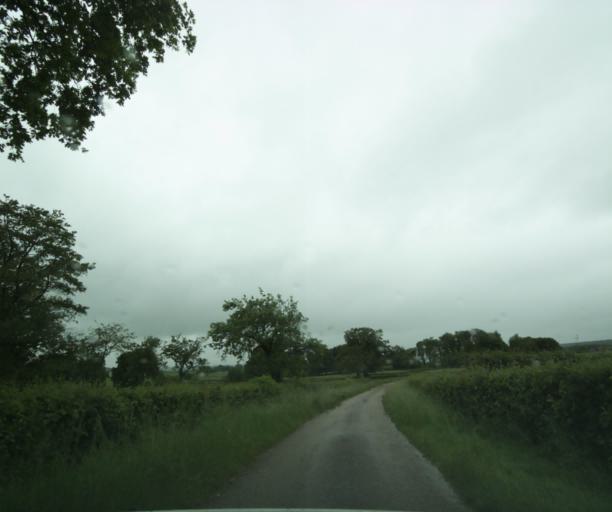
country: FR
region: Bourgogne
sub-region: Departement de Saone-et-Loire
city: Saint-Vallier
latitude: 46.5387
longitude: 4.3943
